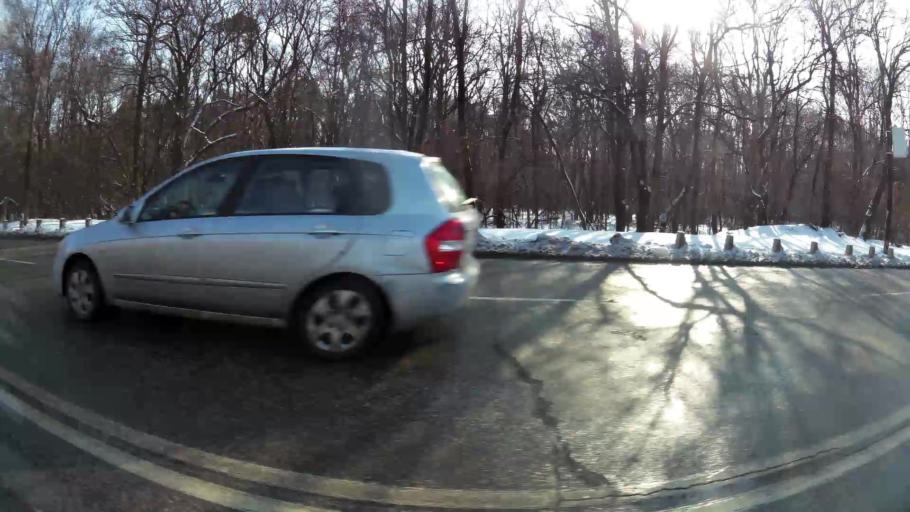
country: BG
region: Sofia-Capital
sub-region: Stolichna Obshtina
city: Sofia
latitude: 42.6667
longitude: 23.3394
